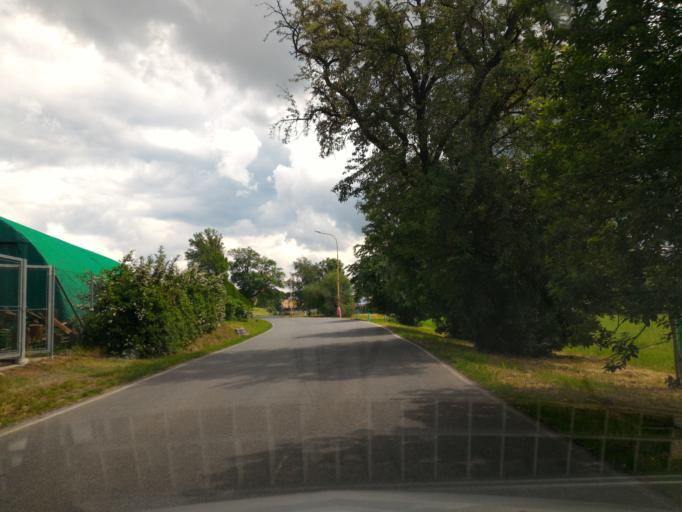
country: CZ
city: Hradek nad Nisou
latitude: 50.8555
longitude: 14.8369
